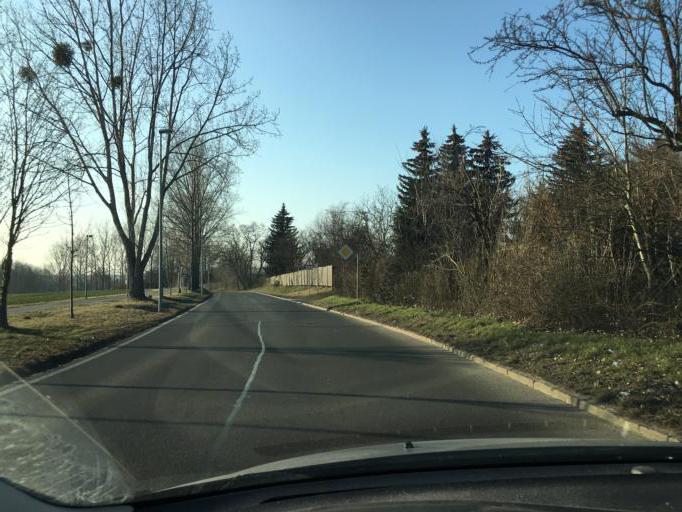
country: DE
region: Saxony
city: Grossposna
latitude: 51.3116
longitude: 12.4499
